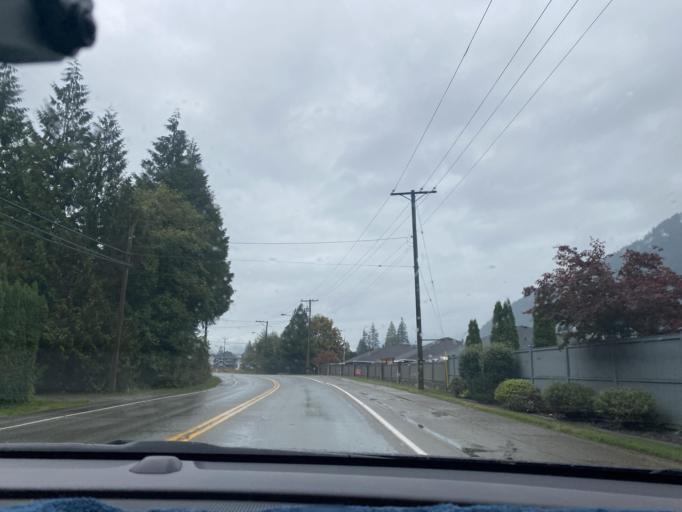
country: CA
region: British Columbia
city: Agassiz
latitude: 49.2902
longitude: -121.7800
